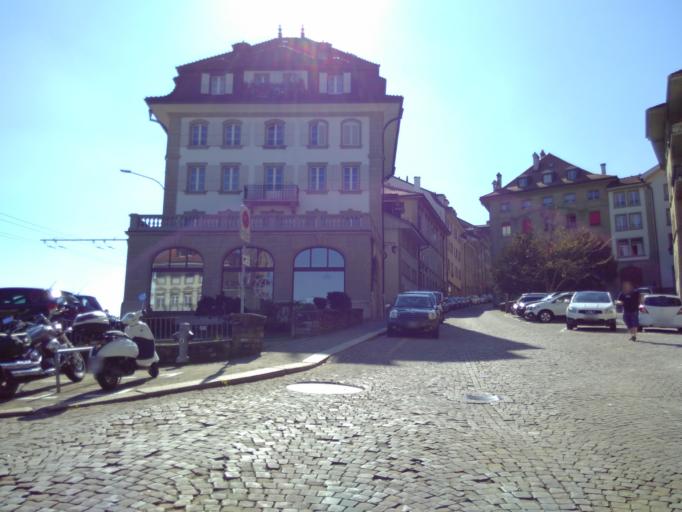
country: CH
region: Fribourg
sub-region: Sarine District
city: Fribourg
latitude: 46.8055
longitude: 7.1599
